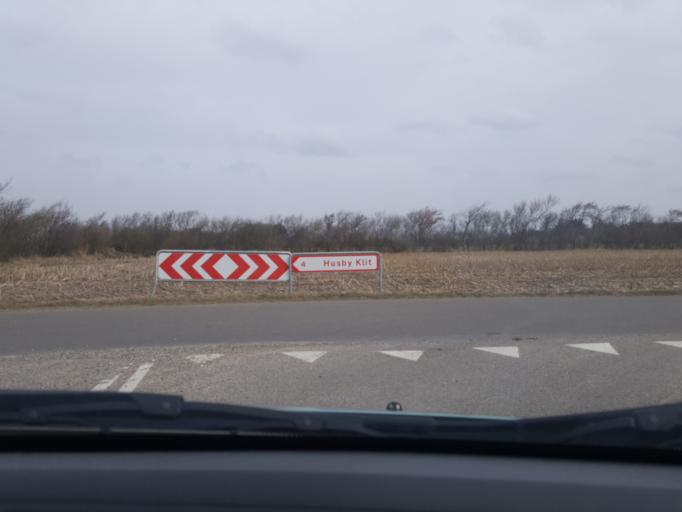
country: DK
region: Central Jutland
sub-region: Ringkobing-Skjern Kommune
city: Ringkobing
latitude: 56.2028
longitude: 8.1874
